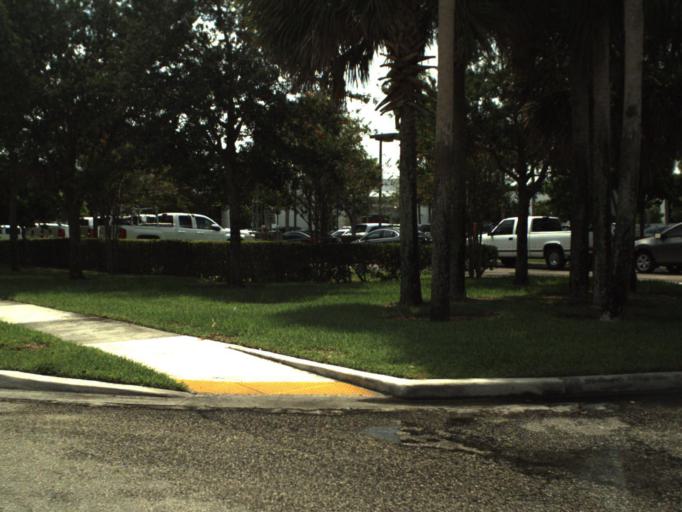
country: US
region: Florida
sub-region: Broward County
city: Tamarac
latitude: 26.2392
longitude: -80.2501
